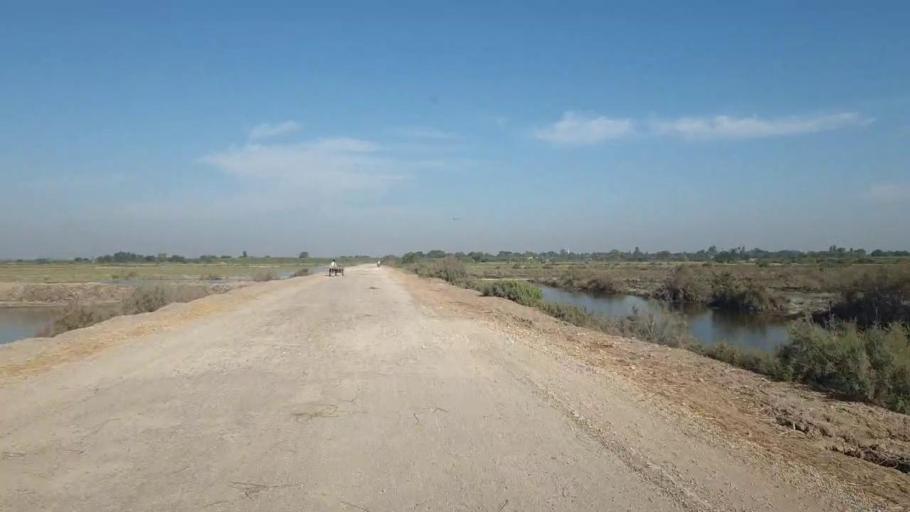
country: PK
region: Sindh
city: Talhar
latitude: 24.9195
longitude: 68.8013
